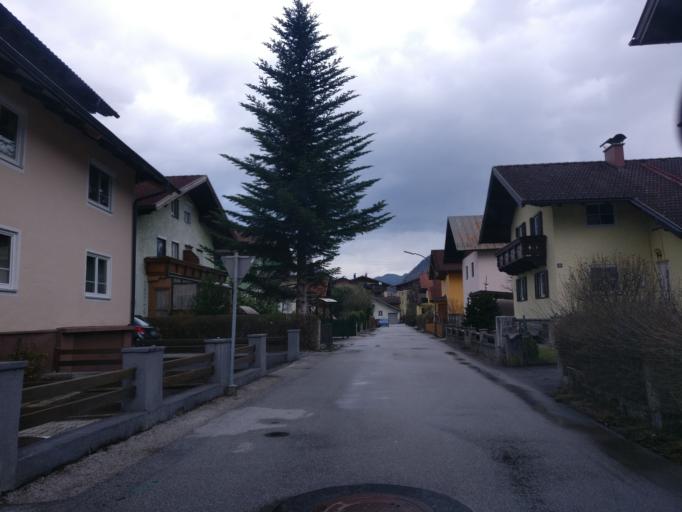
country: AT
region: Salzburg
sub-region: Politischer Bezirk Hallein
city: Golling an der Salzach
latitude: 47.5920
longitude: 13.1648
